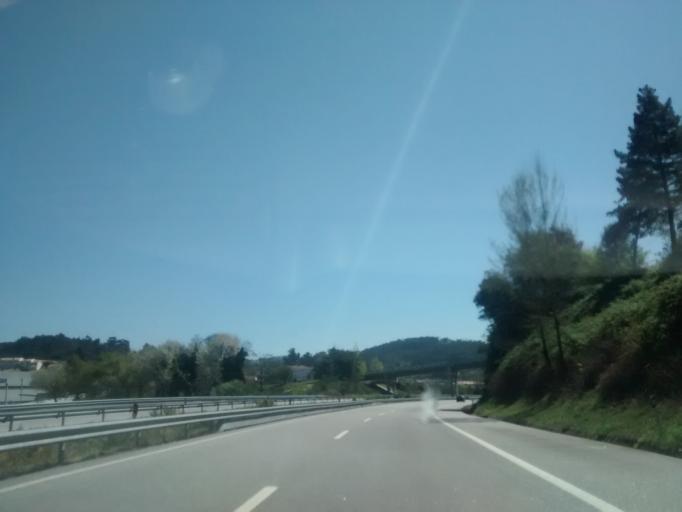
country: PT
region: Braga
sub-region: Guimaraes
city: Candoso
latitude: 41.4190
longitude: -8.3268
